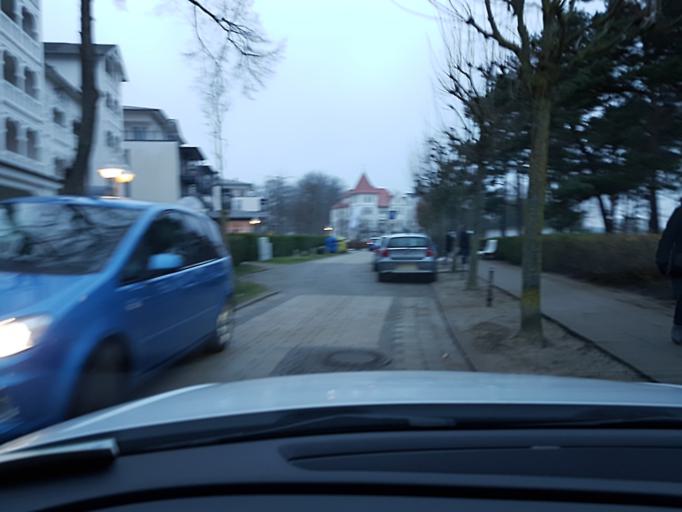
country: DE
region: Mecklenburg-Vorpommern
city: Ostseebad Binz
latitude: 54.3987
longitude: 13.6215
